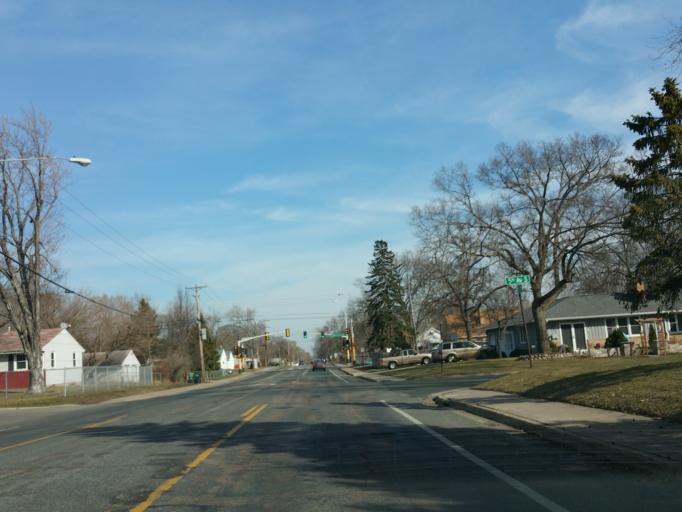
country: US
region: Minnesota
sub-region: Hennepin County
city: Bloomington
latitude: 44.8479
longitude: -93.2699
